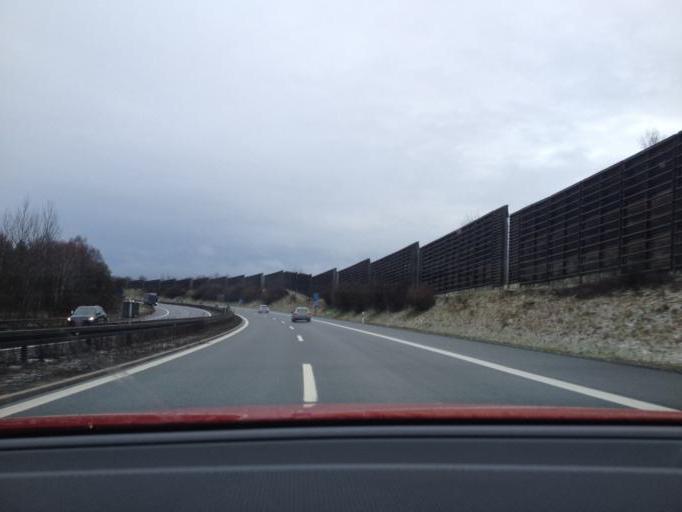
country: DE
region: Bavaria
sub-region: Upper Franconia
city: Selb
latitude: 50.1766
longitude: 12.1188
